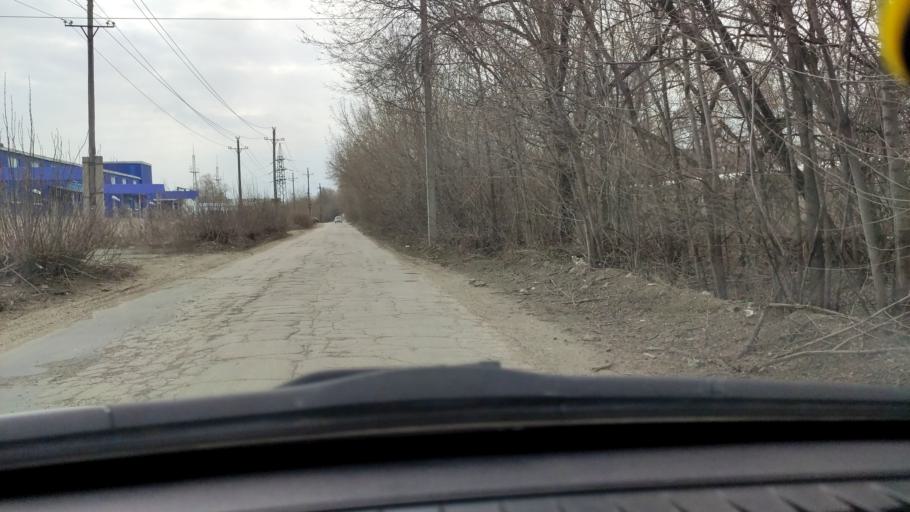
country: RU
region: Samara
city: Tol'yatti
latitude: 53.5232
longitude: 49.4557
